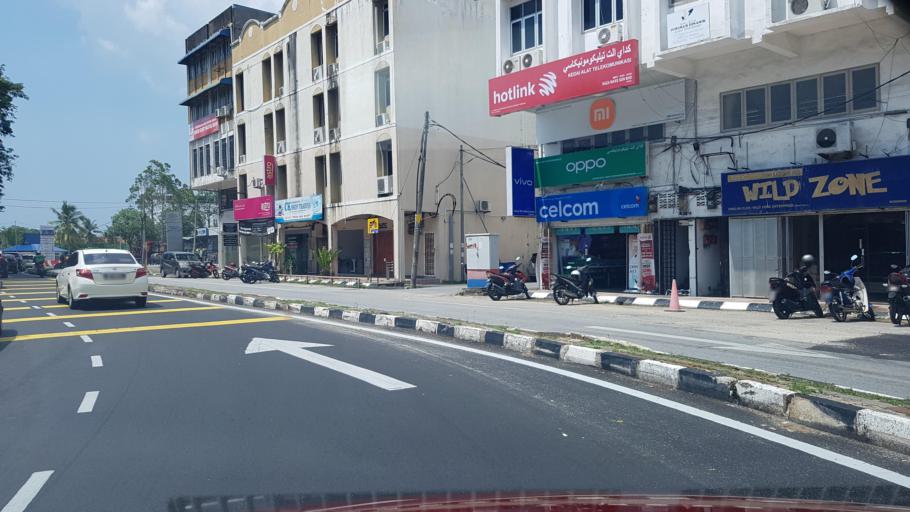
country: MY
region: Terengganu
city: Kuala Terengganu
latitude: 5.3280
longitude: 103.1374
